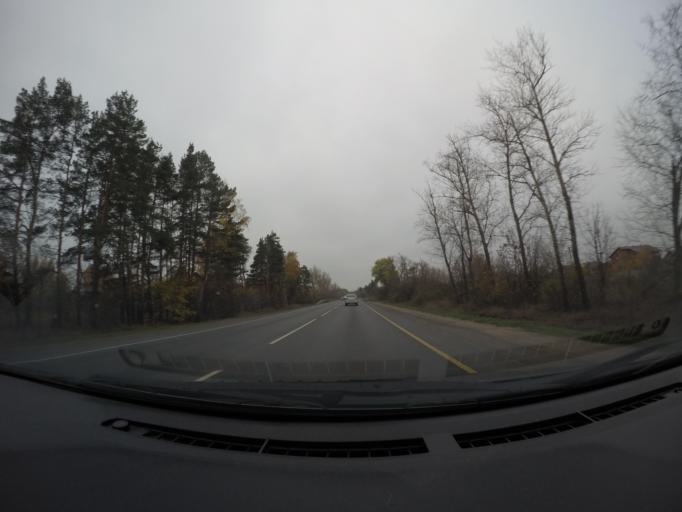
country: RU
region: Moskovskaya
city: Malyshevo
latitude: 55.4595
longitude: 38.3312
